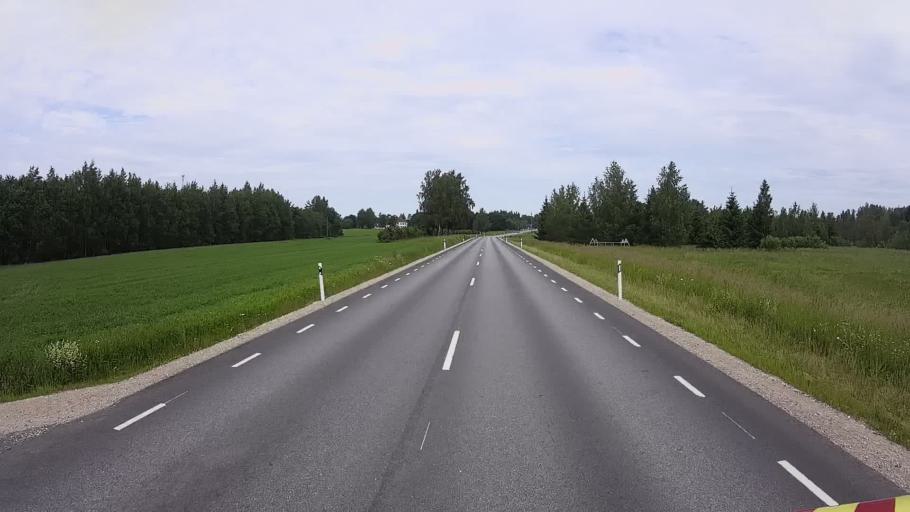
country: EE
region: Viljandimaa
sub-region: Viljandi linn
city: Viljandi
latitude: 58.2355
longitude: 25.5983
